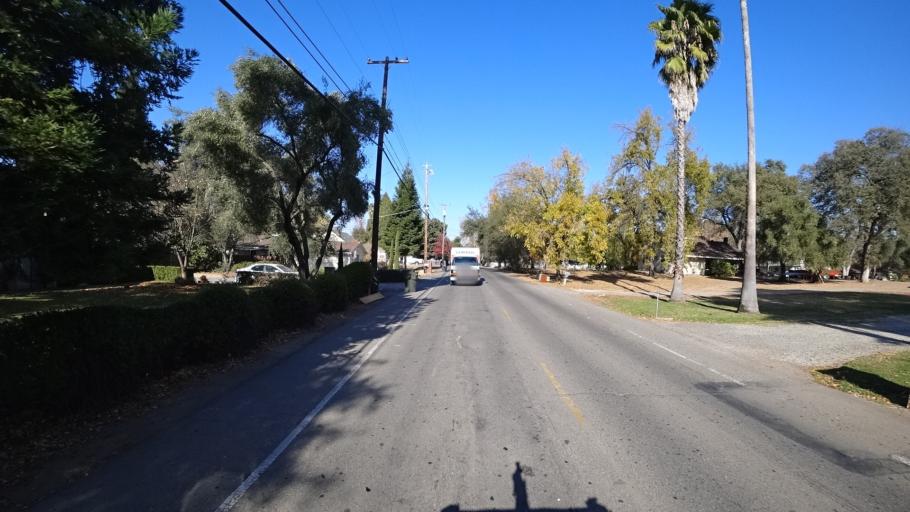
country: US
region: California
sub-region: Sacramento County
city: Citrus Heights
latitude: 38.6958
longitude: -121.2812
